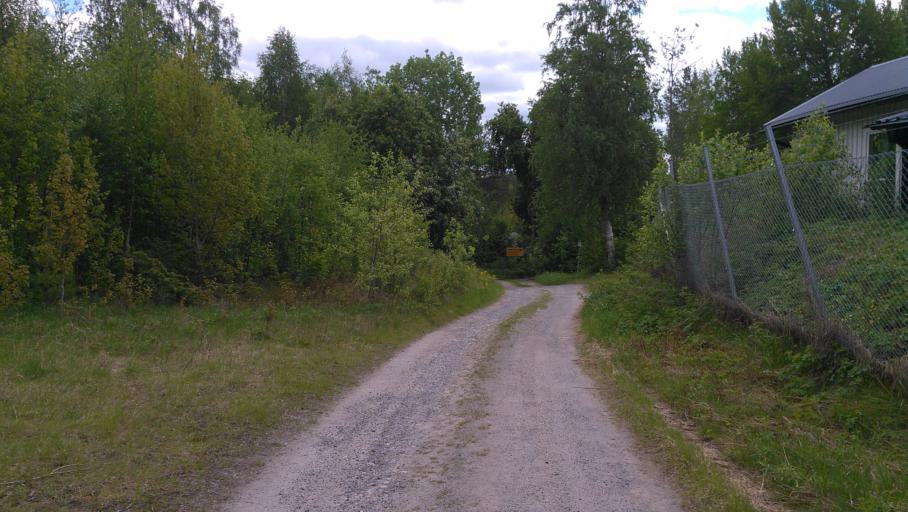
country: SE
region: Vaesterbotten
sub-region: Umea Kommun
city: Roback
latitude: 63.8807
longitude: 20.0234
